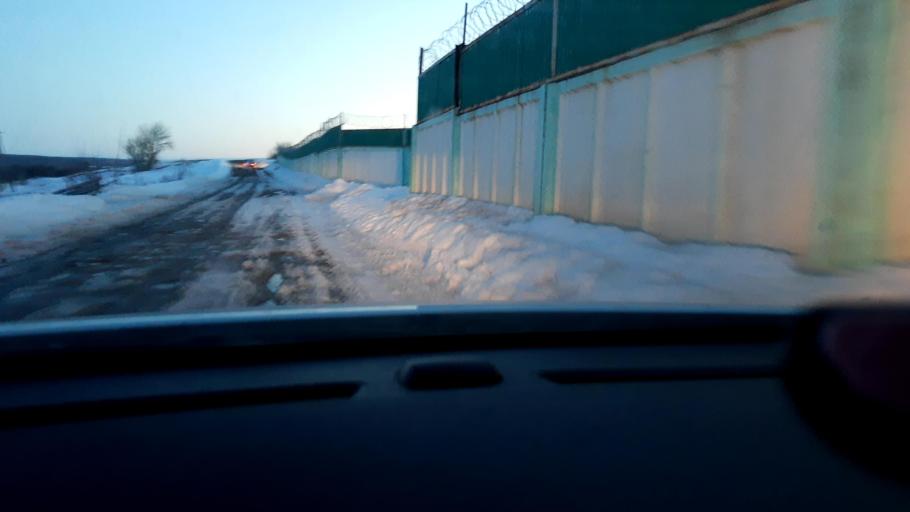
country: RU
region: Bashkortostan
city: Avdon
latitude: 54.3885
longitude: 55.6962
